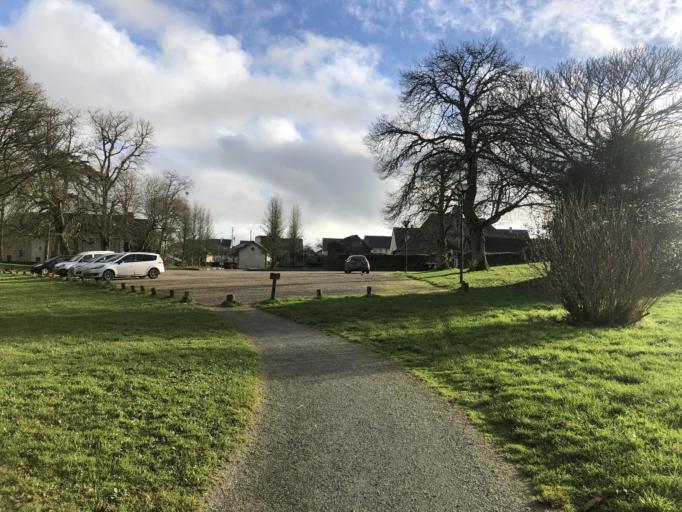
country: FR
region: Pays de la Loire
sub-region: Departement de Maine-et-Loire
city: Le Plessis-Mace
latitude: 47.5443
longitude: -0.6771
